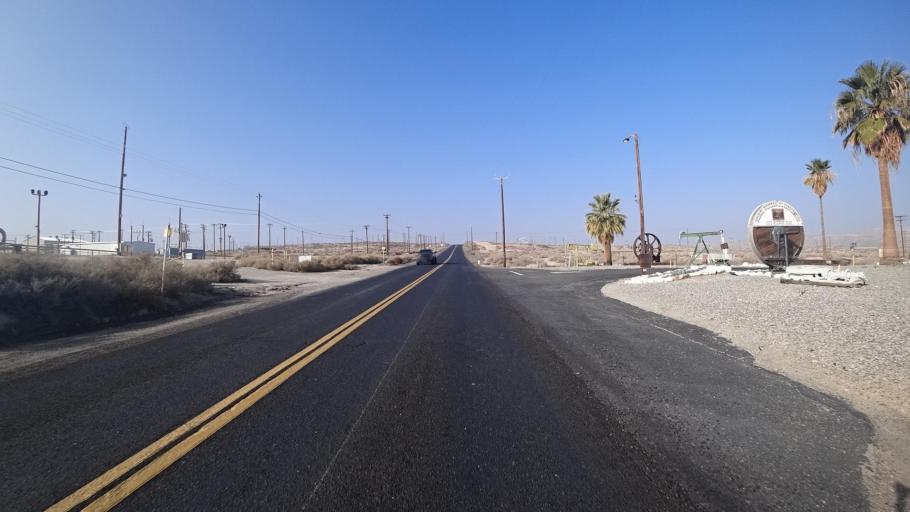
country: US
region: California
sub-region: Kern County
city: Ford City
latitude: 35.1806
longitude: -119.4608
